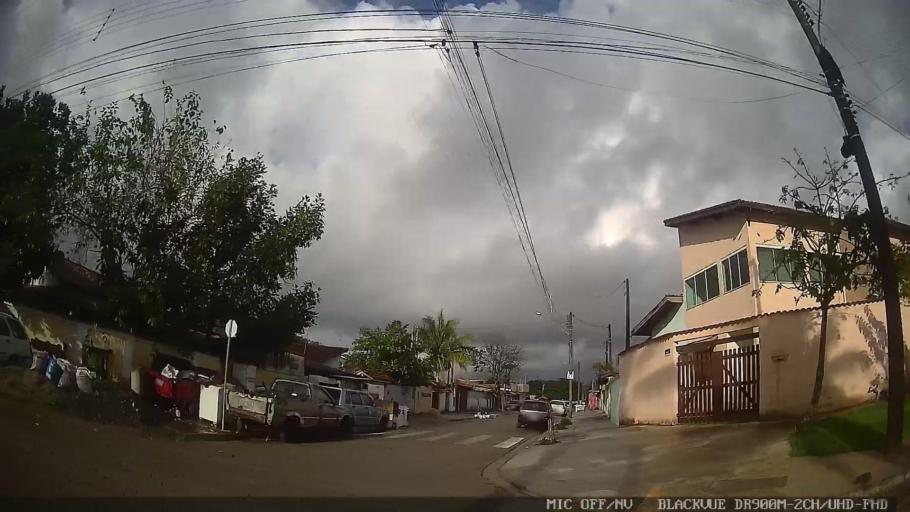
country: BR
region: Sao Paulo
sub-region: Itanhaem
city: Itanhaem
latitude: -24.2078
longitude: -46.8764
